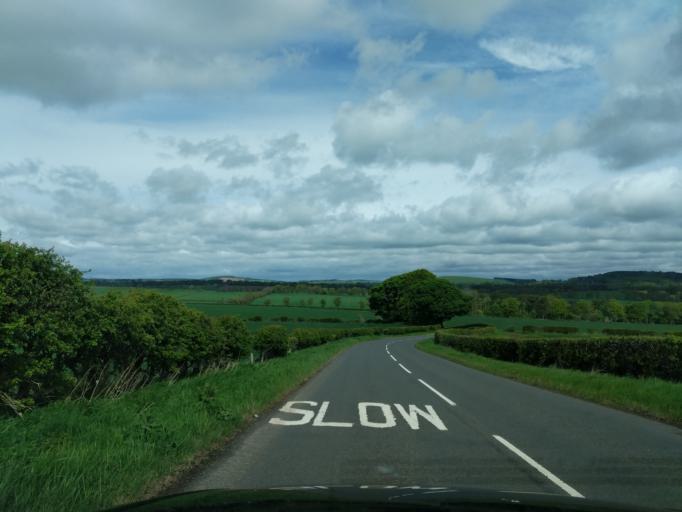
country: GB
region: Scotland
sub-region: The Scottish Borders
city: Saint Boswells
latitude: 55.6210
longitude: -2.5632
